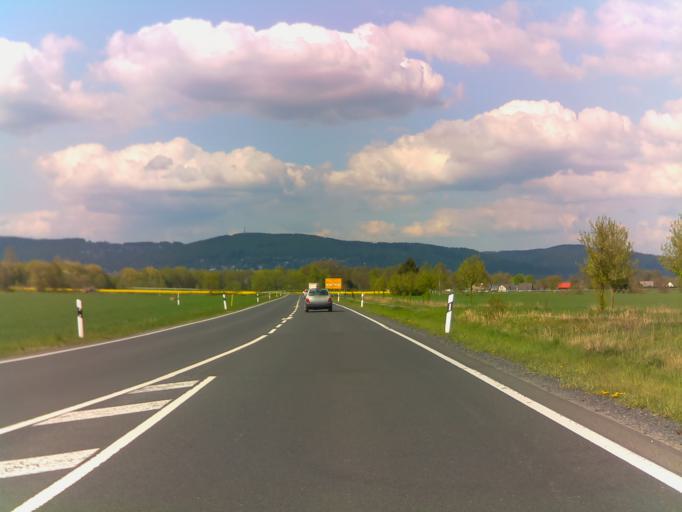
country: DE
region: Bavaria
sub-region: Upper Franconia
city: Ebersdorf
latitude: 50.3213
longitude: 11.1601
